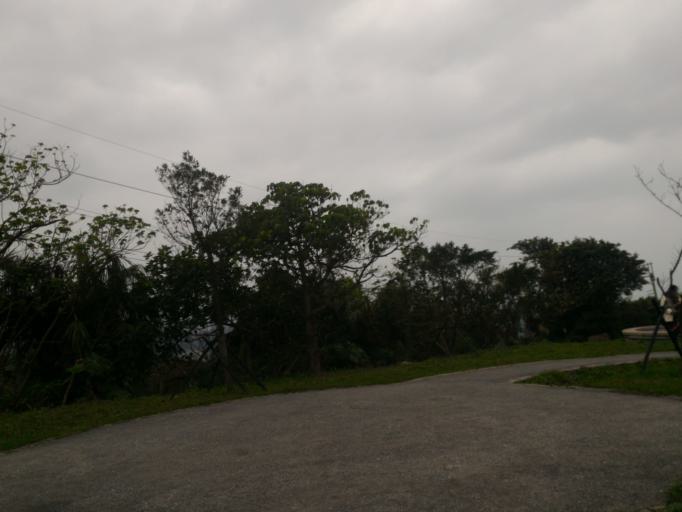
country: TW
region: Taiwan
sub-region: Keelung
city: Keelung
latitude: 25.1370
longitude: 121.7579
